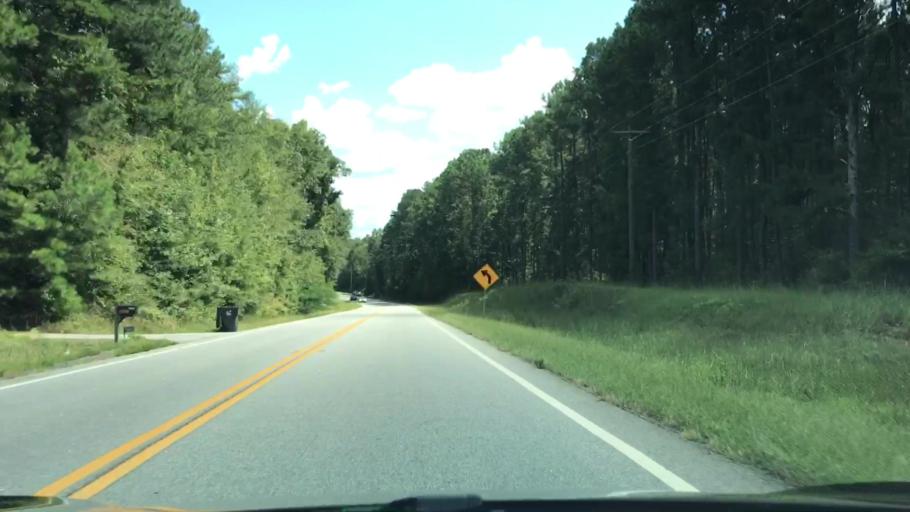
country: US
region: Georgia
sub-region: Greene County
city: Greensboro
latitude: 33.6745
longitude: -83.2664
